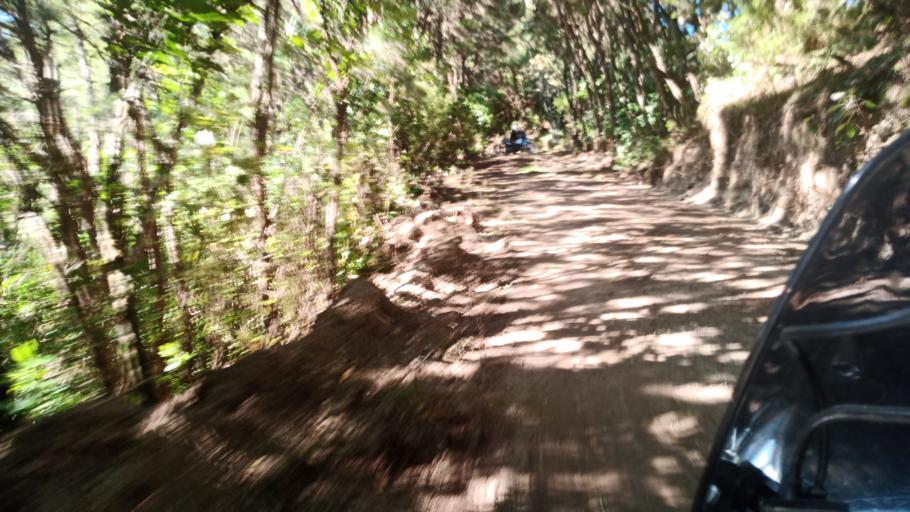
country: NZ
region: Hawke's Bay
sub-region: Wairoa District
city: Wairoa
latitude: -38.9998
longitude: 177.0630
